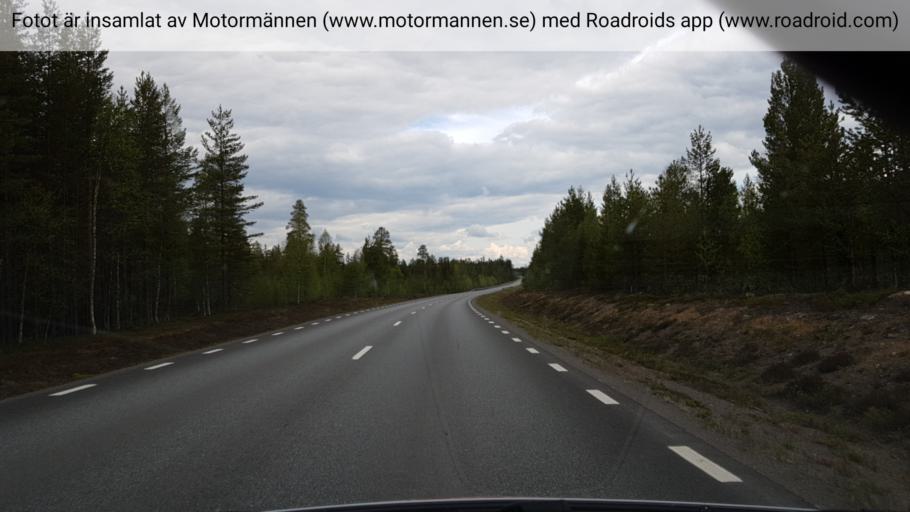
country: SE
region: Norrbotten
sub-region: Arvidsjaurs Kommun
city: Arvidsjaur
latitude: 65.5188
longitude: 19.2657
